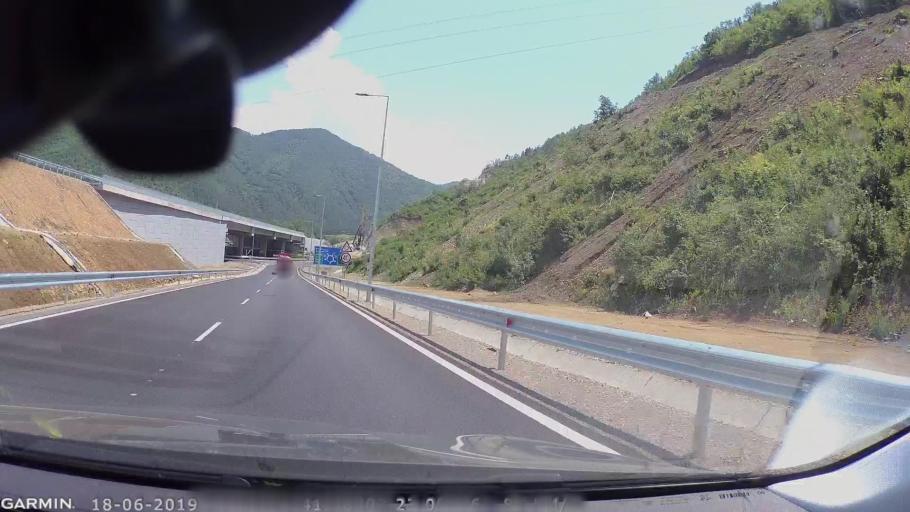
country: BG
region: Blagoevgrad
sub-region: Obshtina Blagoevgrad
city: Blagoevgrad
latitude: 41.9626
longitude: 23.0975
